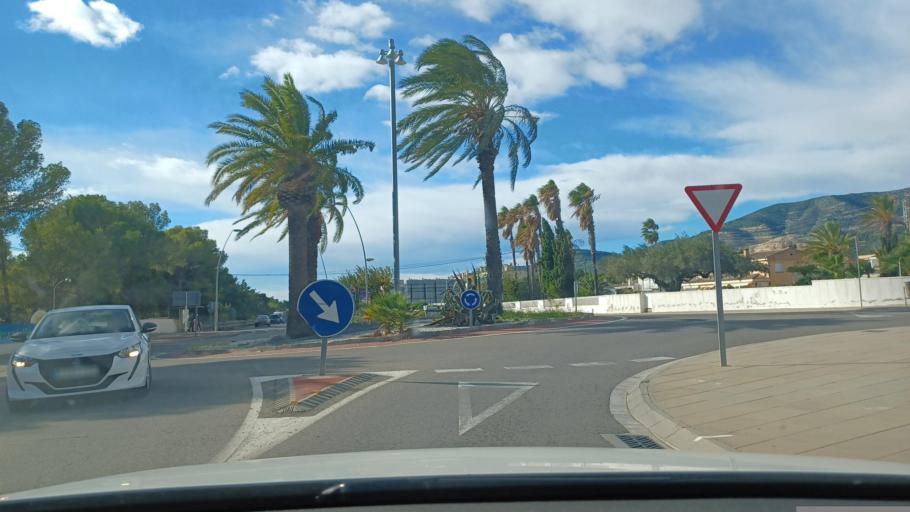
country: ES
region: Catalonia
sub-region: Provincia de Tarragona
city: Sant Carles de la Rapita
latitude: 40.5956
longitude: 0.5703
